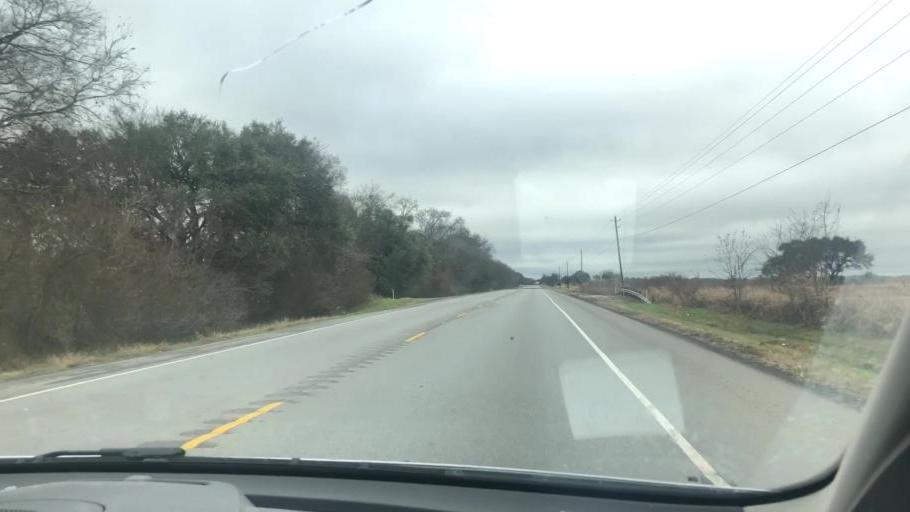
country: US
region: Texas
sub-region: Matagorda County
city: Bay City
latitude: 29.0755
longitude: -95.9725
